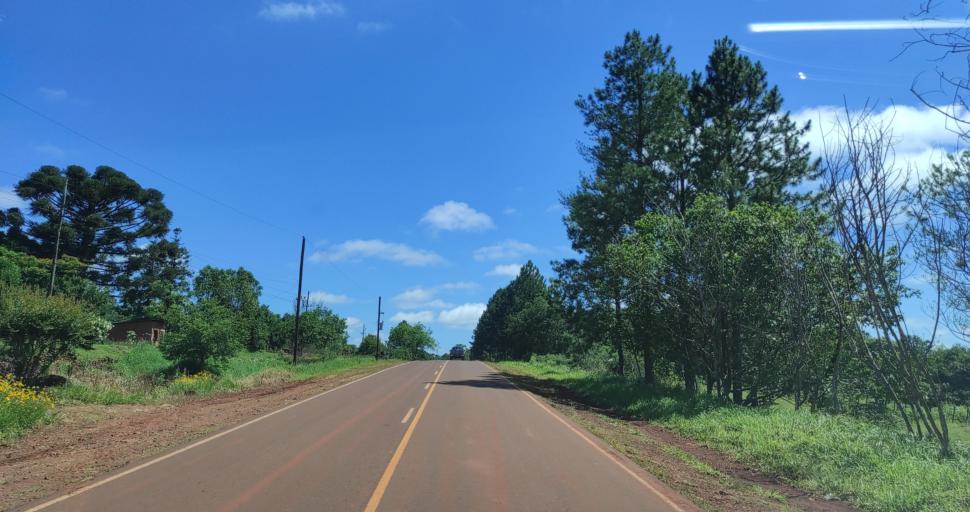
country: AR
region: Misiones
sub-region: Departamento de Veinticinco de Mayo
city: Veinticinco de Mayo
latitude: -27.3989
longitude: -54.7501
